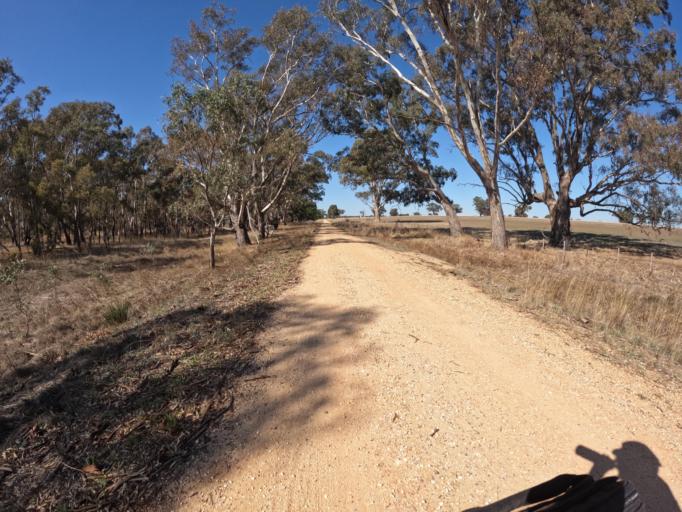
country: AU
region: Victoria
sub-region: Greater Bendigo
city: Kennington
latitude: -36.8337
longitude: 144.5949
